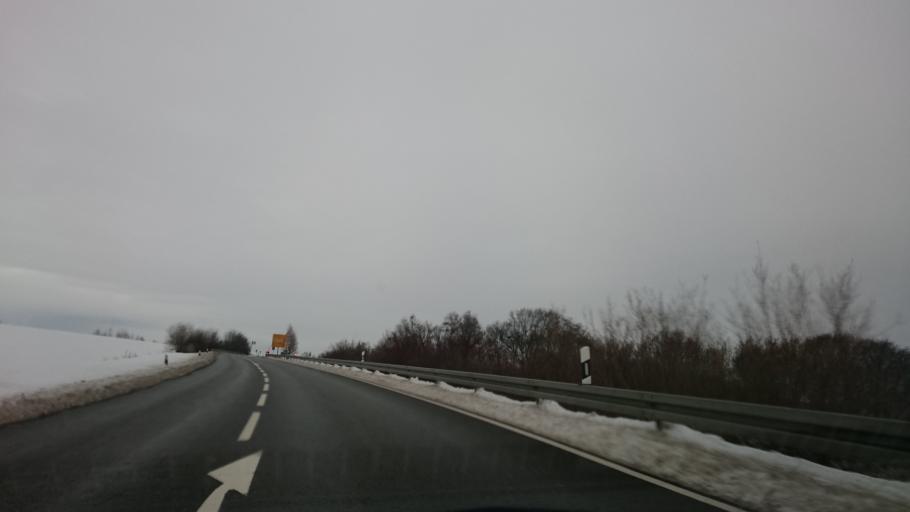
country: DE
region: Saxony
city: Mulsen
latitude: 50.7476
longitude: 12.5982
